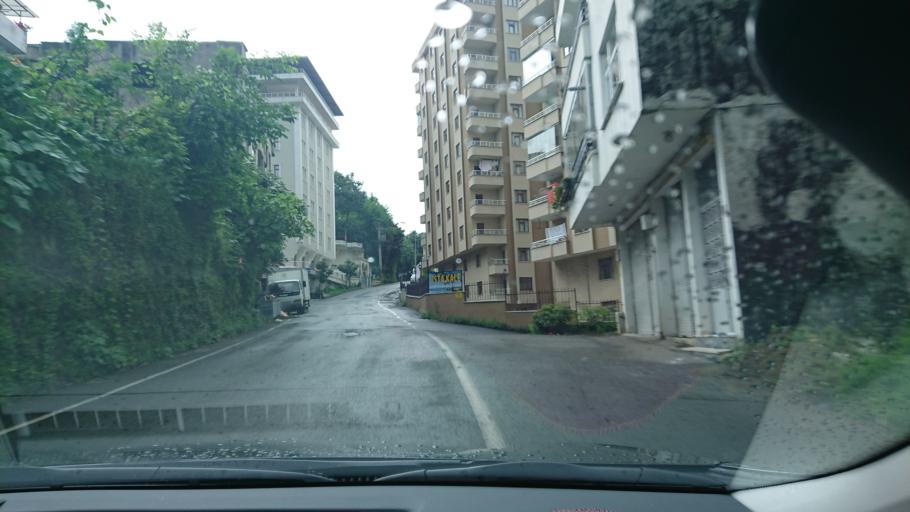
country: TR
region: Rize
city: Rize
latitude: 41.0255
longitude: 40.5113
